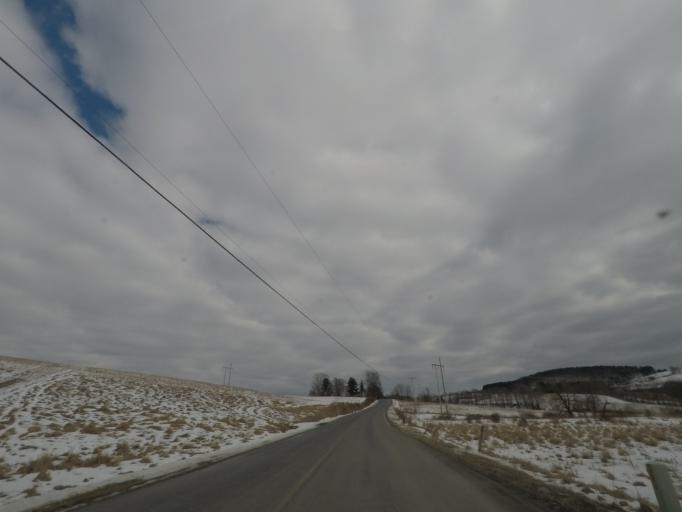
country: US
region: New York
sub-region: Rensselaer County
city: Hoosick Falls
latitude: 42.8753
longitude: -73.4122
